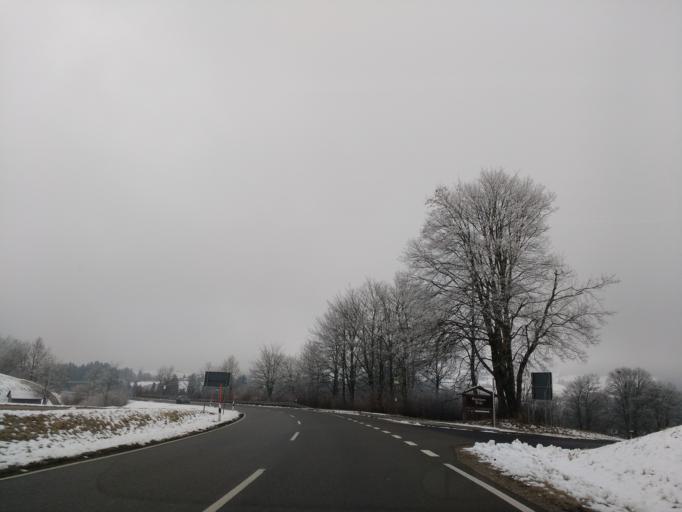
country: DE
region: Bavaria
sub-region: Swabia
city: Nesselwang
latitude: 47.6343
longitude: 10.4714
